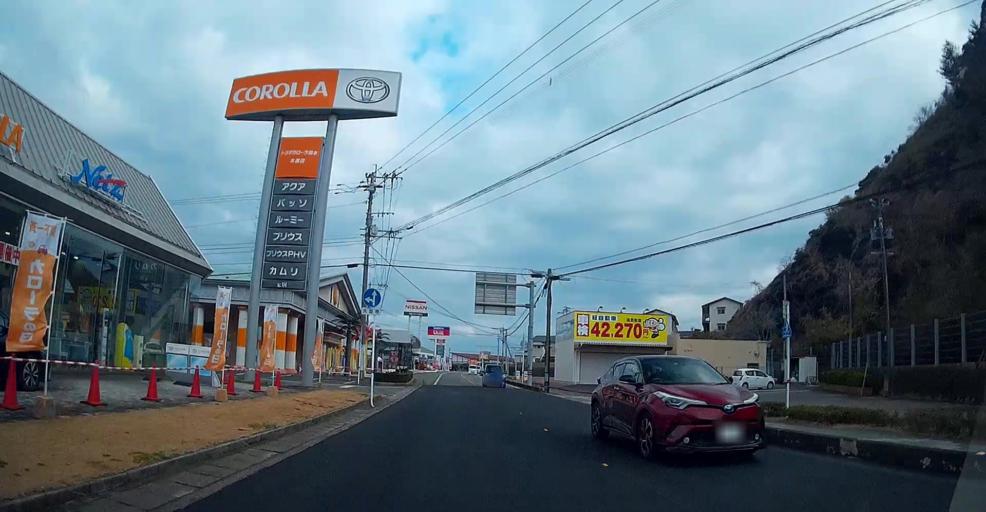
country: JP
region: Kumamoto
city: Hondo
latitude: 32.4502
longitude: 130.2069
